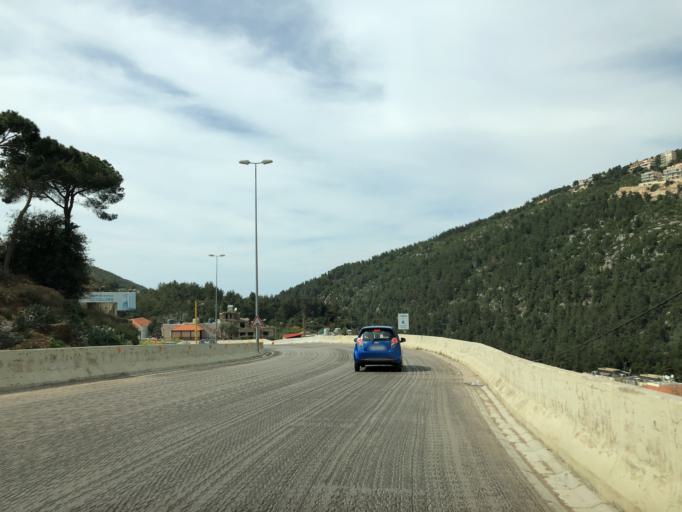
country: LB
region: Mont-Liban
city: Bhamdoun el Mhatta
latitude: 33.8916
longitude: 35.6598
